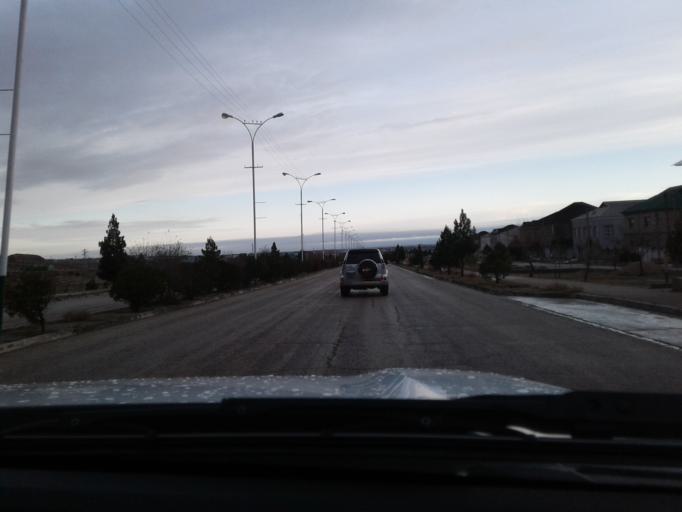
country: TM
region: Balkan
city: Balkanabat
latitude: 39.5368
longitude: 54.3512
